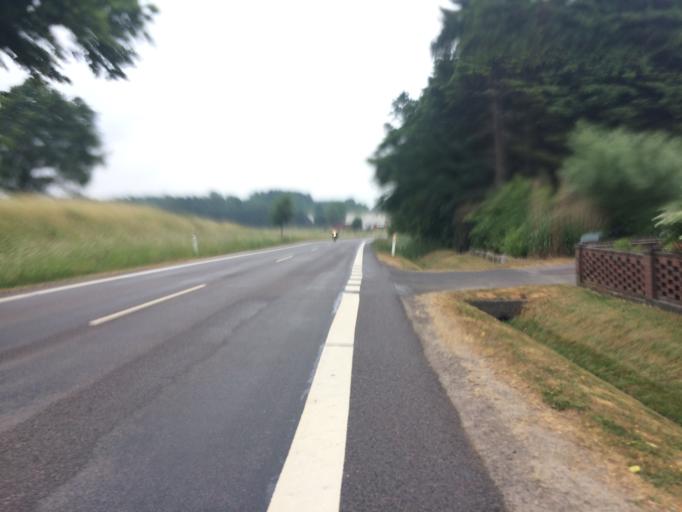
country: DK
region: Capital Region
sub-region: Bornholm Kommune
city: Akirkeby
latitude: 55.1479
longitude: 14.8799
